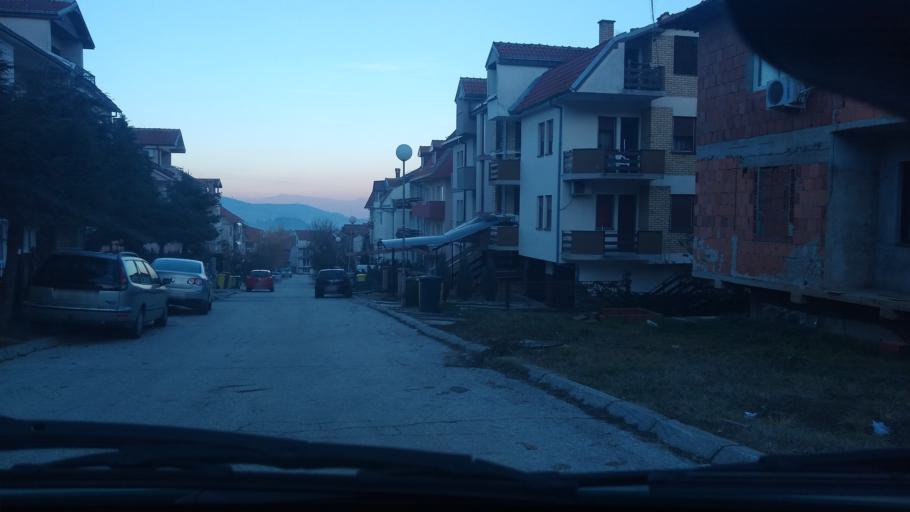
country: MK
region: Bitola
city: Bitola
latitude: 41.0225
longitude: 21.3038
